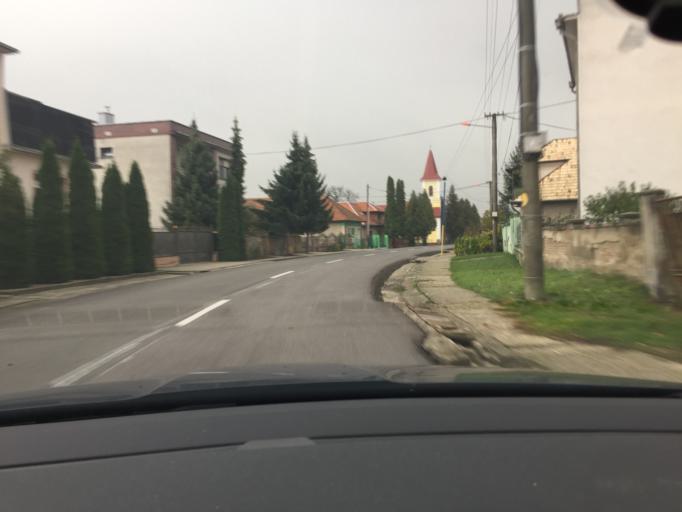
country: SK
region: Nitriansky
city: Zeliezovce
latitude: 47.9933
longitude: 18.7743
